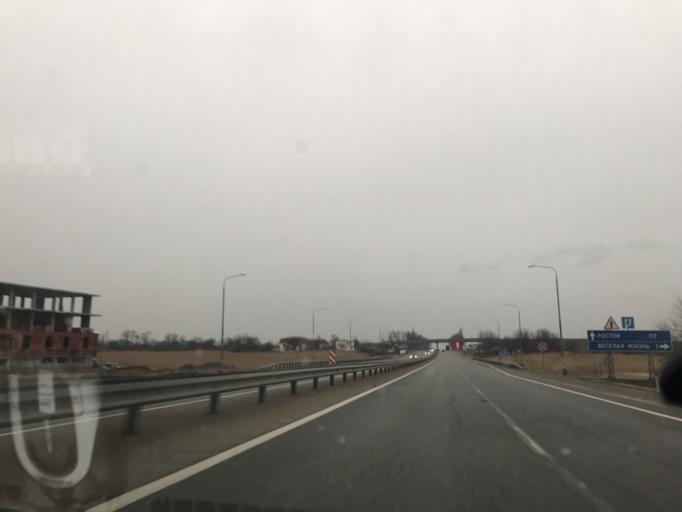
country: RU
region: Krasnodarskiy
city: Pavlovskaya
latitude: 46.2214
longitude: 39.8315
